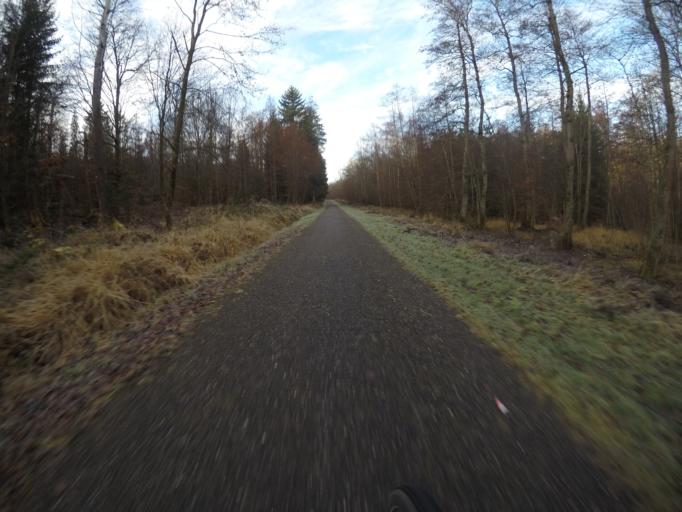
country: DE
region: Baden-Wuerttemberg
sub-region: Regierungsbezirk Stuttgart
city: Sindelfingen
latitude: 48.7239
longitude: 9.0319
